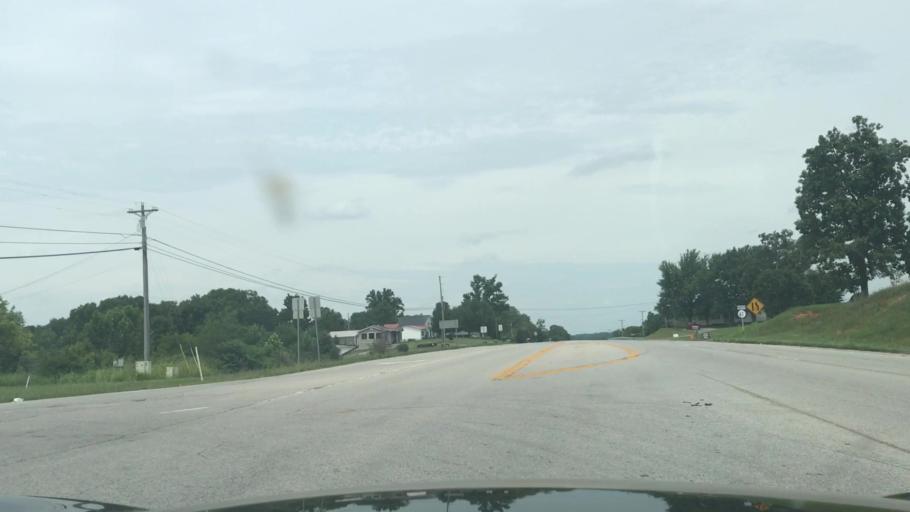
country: US
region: Kentucky
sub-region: Green County
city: Greensburg
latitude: 37.2845
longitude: -85.5176
